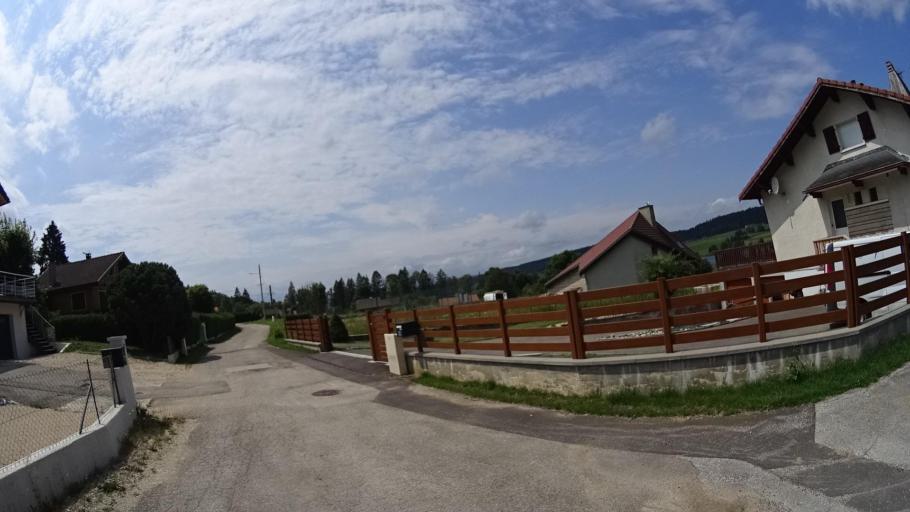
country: FR
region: Franche-Comte
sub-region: Departement du Doubs
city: Les Fourgs
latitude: 46.8165
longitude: 6.3201
